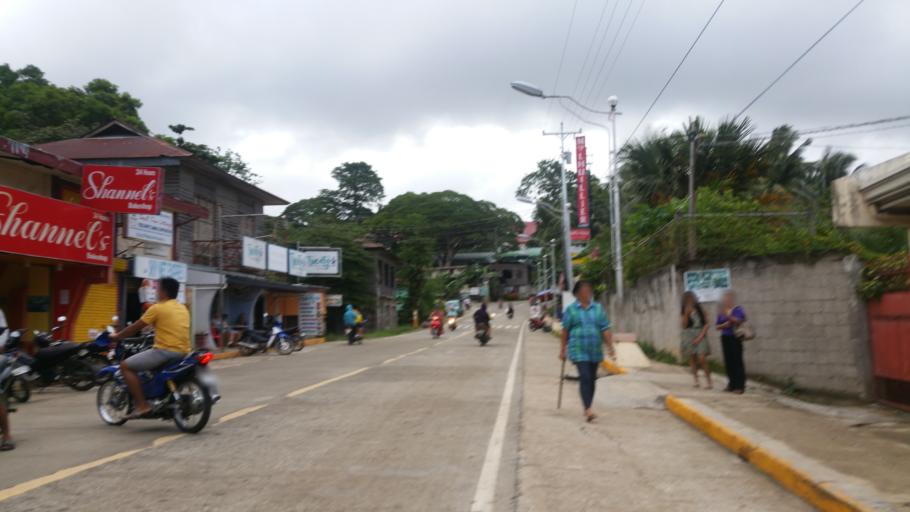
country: PH
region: Central Visayas
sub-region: Province of Siquijor
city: Lazi
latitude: 9.1261
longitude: 123.6352
